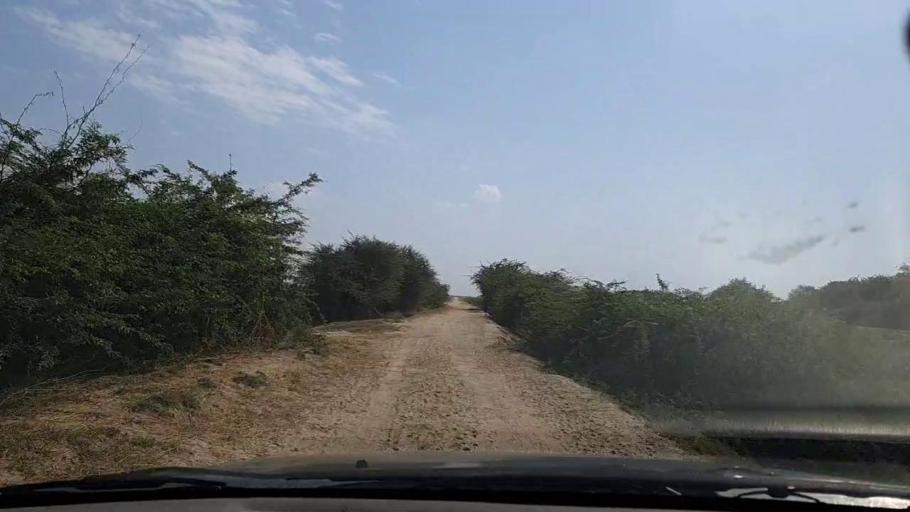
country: PK
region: Sindh
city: Mirpur Batoro
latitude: 24.5572
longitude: 68.2010
